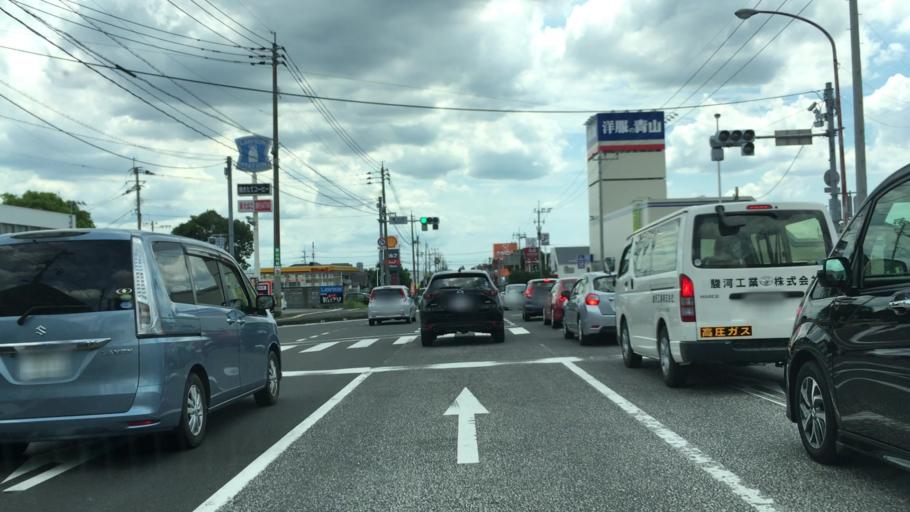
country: JP
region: Saga Prefecture
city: Tosu
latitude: 33.3802
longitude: 130.4991
